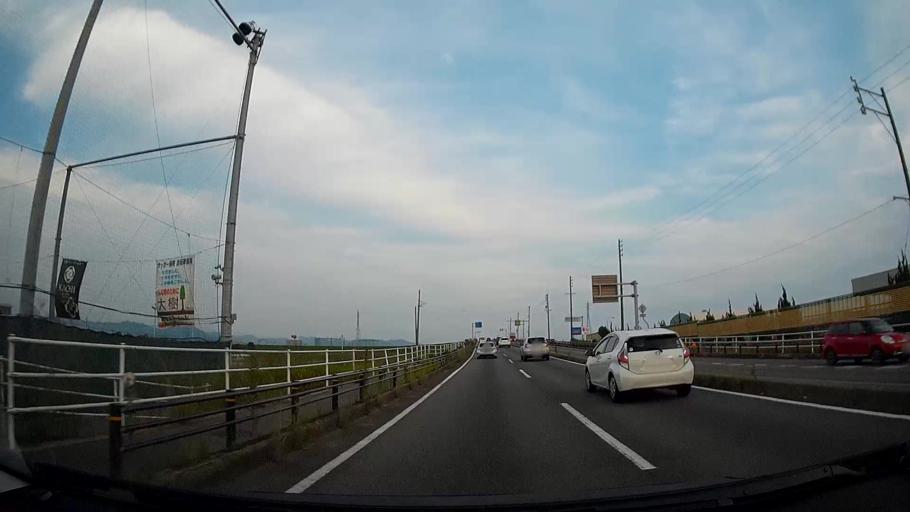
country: JP
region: Aichi
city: Kozakai-cho
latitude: 34.7955
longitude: 137.3687
